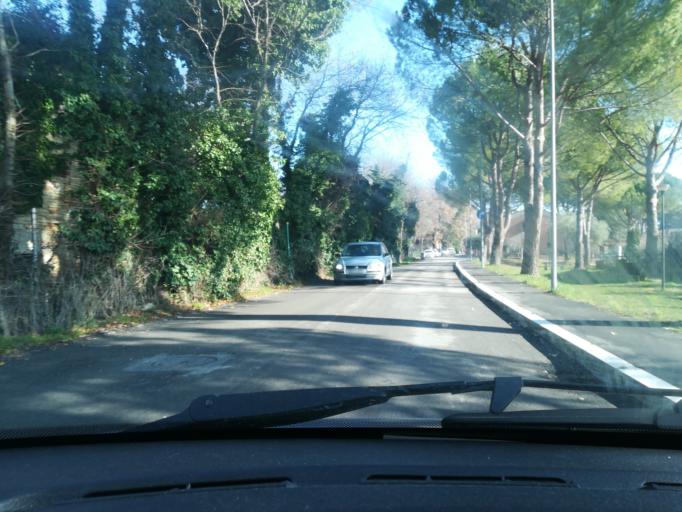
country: IT
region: The Marches
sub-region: Provincia di Macerata
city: Macerata
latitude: 43.2897
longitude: 13.4498
